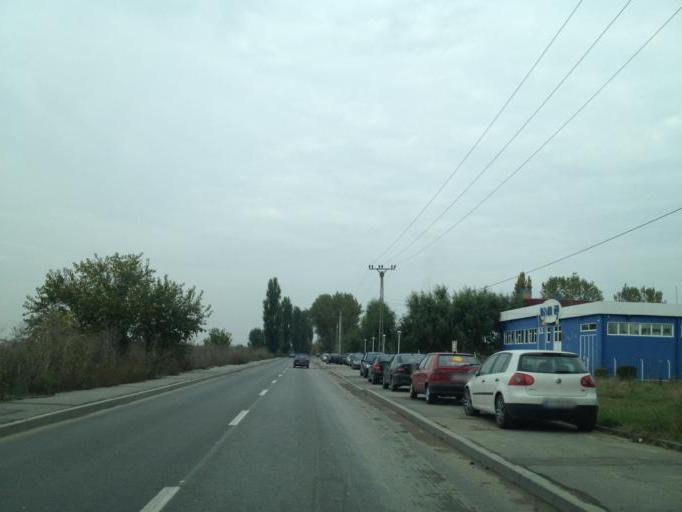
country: RO
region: Dolj
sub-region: Municipiul Craiova
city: Popoveni
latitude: 44.2892
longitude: 23.7933
